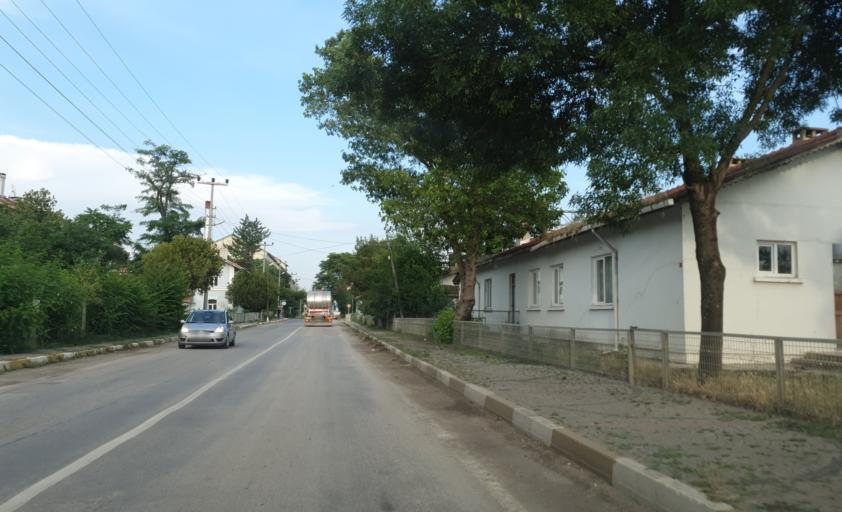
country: TR
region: Kirklareli
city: Babaeski
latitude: 41.3668
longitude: 27.1402
